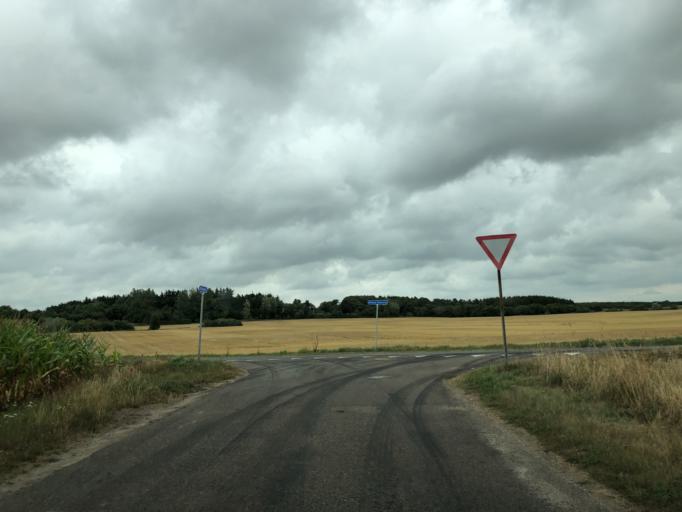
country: DK
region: Central Jutland
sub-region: Ringkobing-Skjern Kommune
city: Videbaek
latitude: 56.0985
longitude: 8.4891
